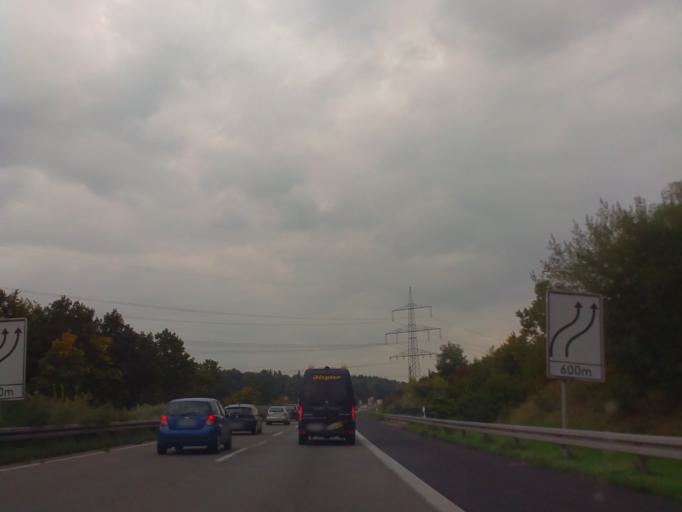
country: DE
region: Hesse
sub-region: Regierungsbezirk Kassel
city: Kunzell
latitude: 50.5168
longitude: 9.7406
